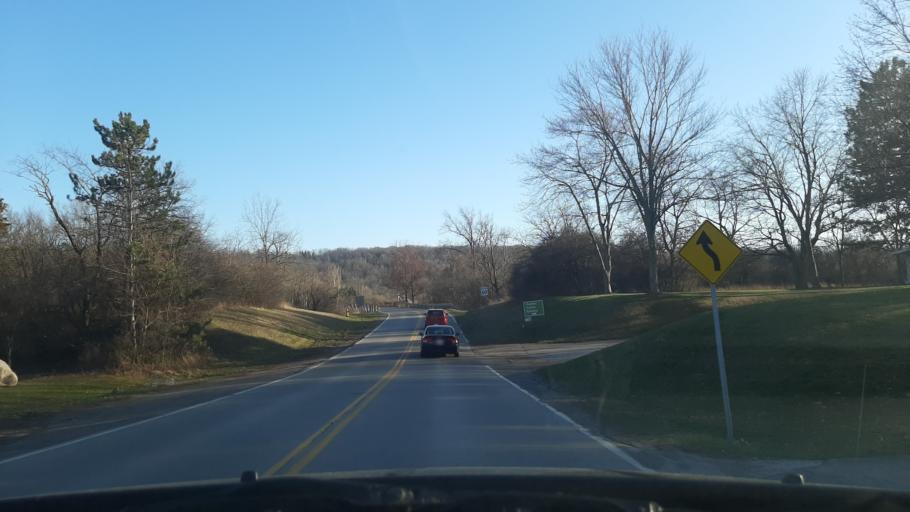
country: US
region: New York
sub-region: Niagara County
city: Lewiston
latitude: 43.1683
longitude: -79.0610
